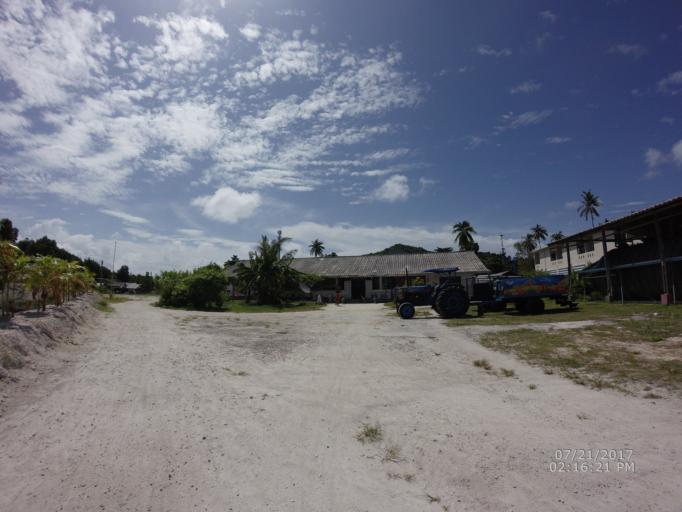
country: TH
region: Phangnga
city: Ban Phru Nai
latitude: 7.7594
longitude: 98.7705
